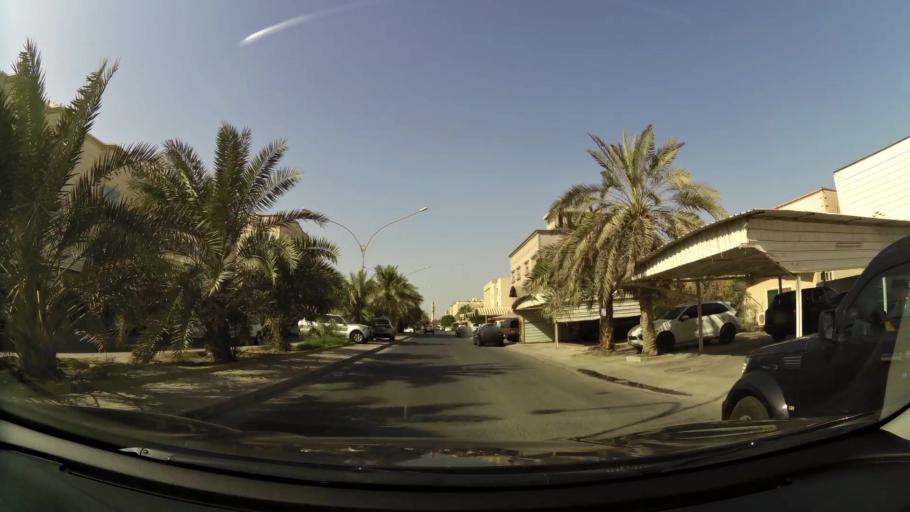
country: KW
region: Muhafazat Hawalli
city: Salwa
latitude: 29.2915
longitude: 48.0779
